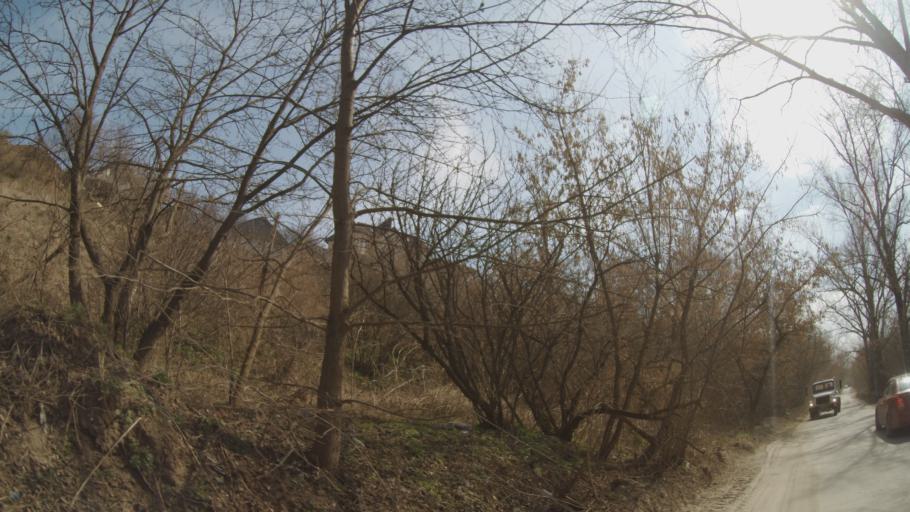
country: RU
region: Nizjnij Novgorod
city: Vyyezdnoye
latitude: 55.3903
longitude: 43.8087
